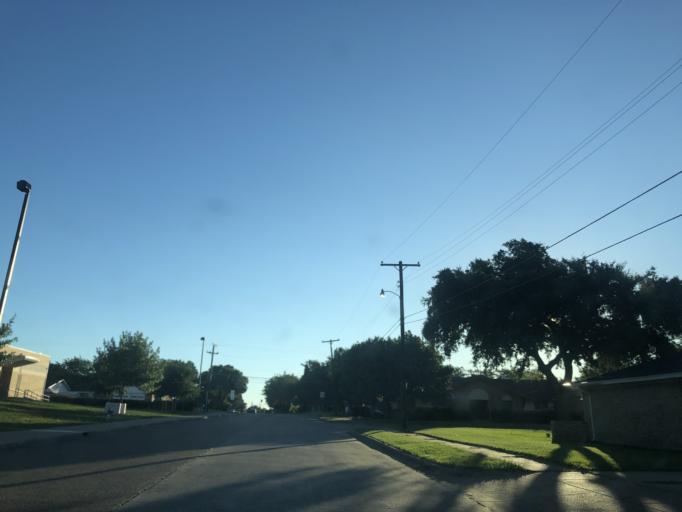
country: US
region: Texas
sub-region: Dallas County
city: Garland
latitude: 32.8342
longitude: -96.6396
